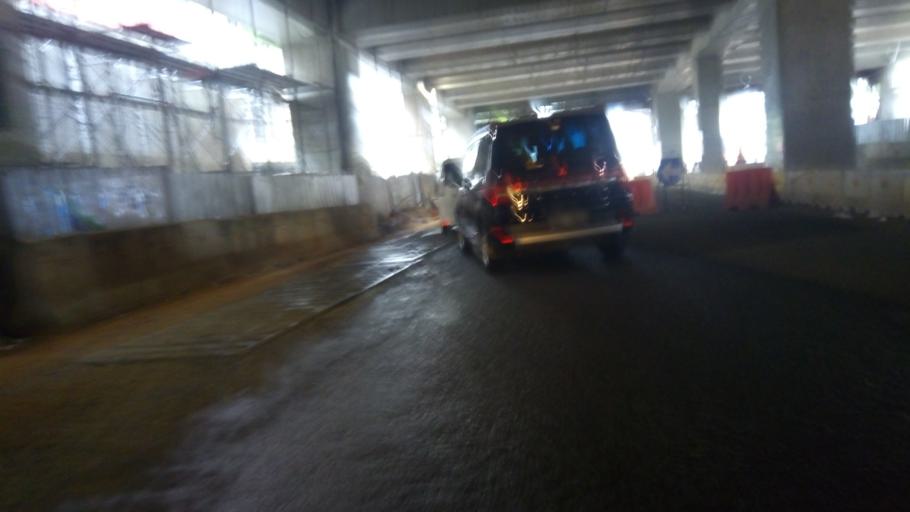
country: ID
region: Jakarta Raya
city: Jakarta
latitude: -6.2446
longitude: 106.7981
